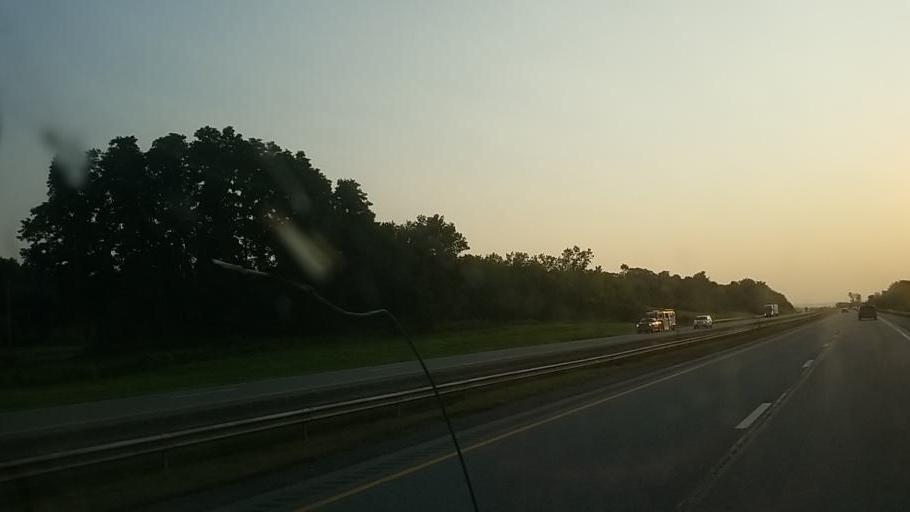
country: US
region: New York
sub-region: Herkimer County
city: Herkimer
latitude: 43.0147
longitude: -74.9495
